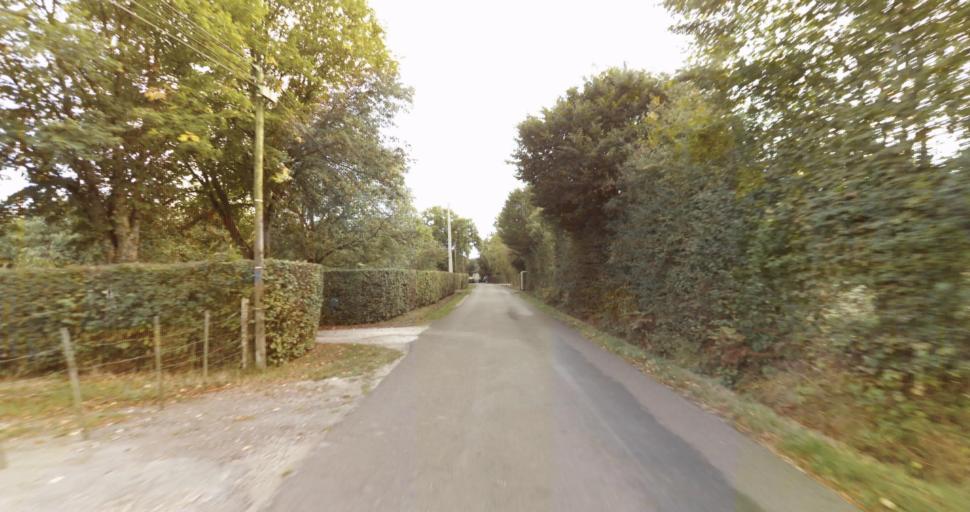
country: FR
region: Lower Normandy
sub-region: Departement de l'Orne
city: Vimoutiers
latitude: 48.8985
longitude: 0.1364
